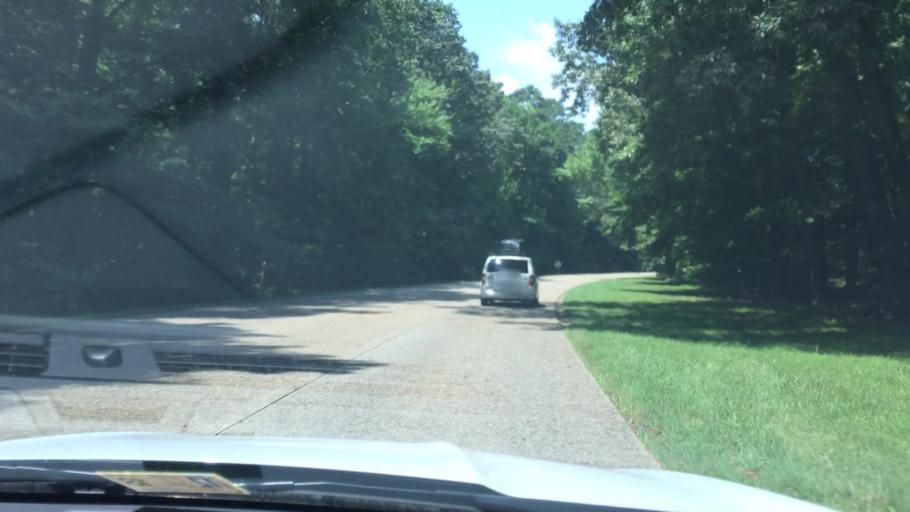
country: US
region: Virginia
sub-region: York County
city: Yorktown
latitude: 37.2297
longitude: -76.5193
